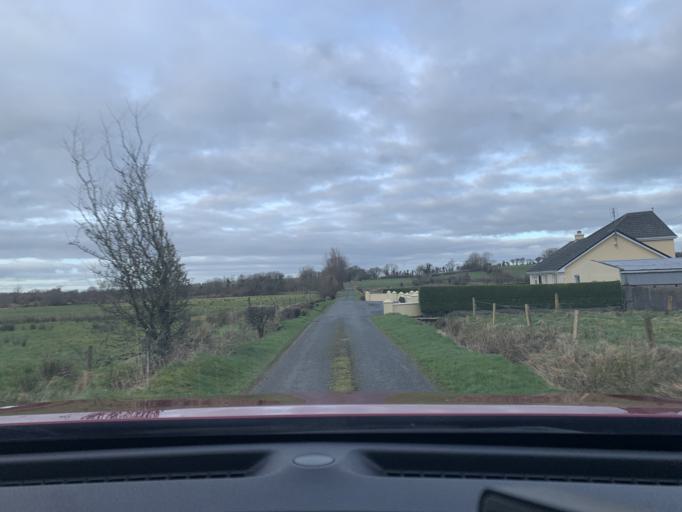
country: IE
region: Connaught
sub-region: Sligo
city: Ballymote
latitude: 54.0103
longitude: -8.5733
